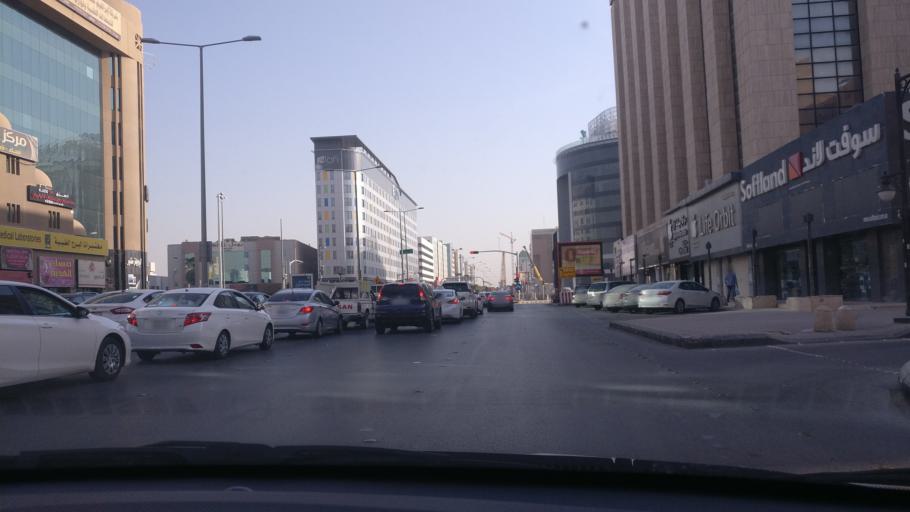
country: SA
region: Ar Riyad
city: Riyadh
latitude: 24.6812
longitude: 46.6913
